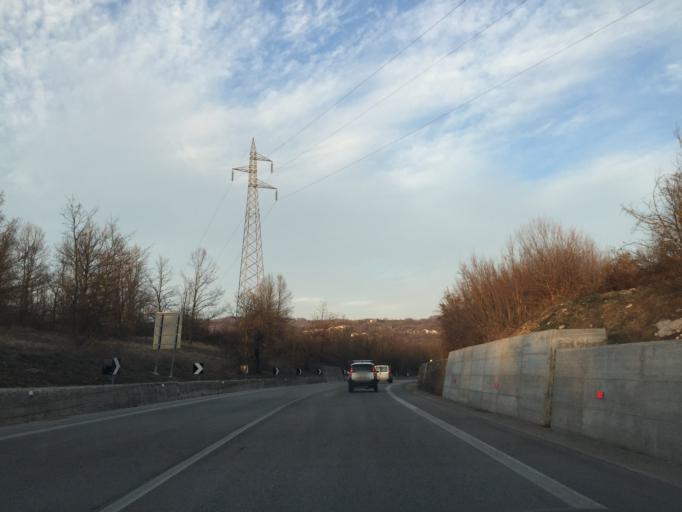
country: IT
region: Molise
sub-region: Provincia di Campobasso
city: Vinchiaturo
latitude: 41.4926
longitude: 14.6040
